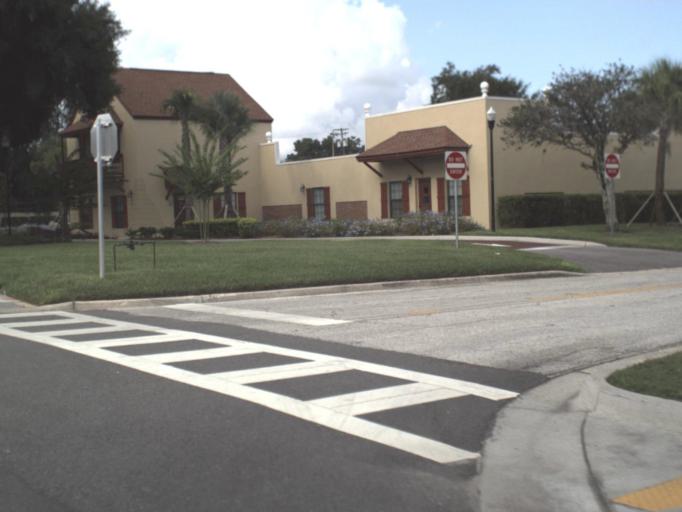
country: US
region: Florida
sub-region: Hillsborough County
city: Temple Terrace
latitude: 28.0385
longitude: -82.3936
